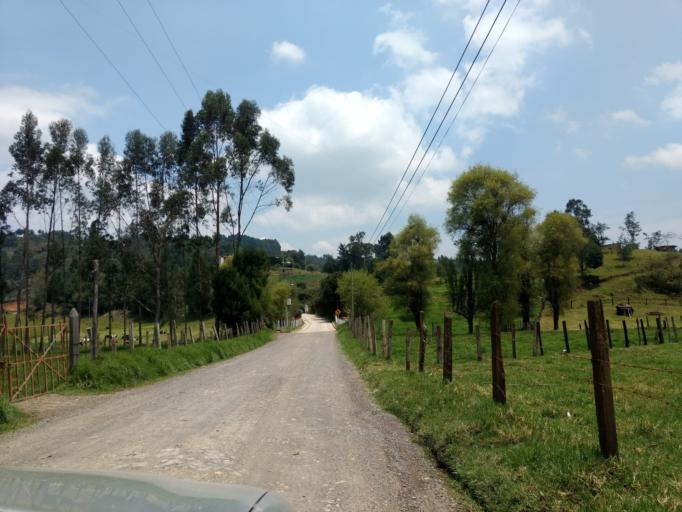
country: CO
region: Boyaca
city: Raquira
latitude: 5.5035
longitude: -73.7118
